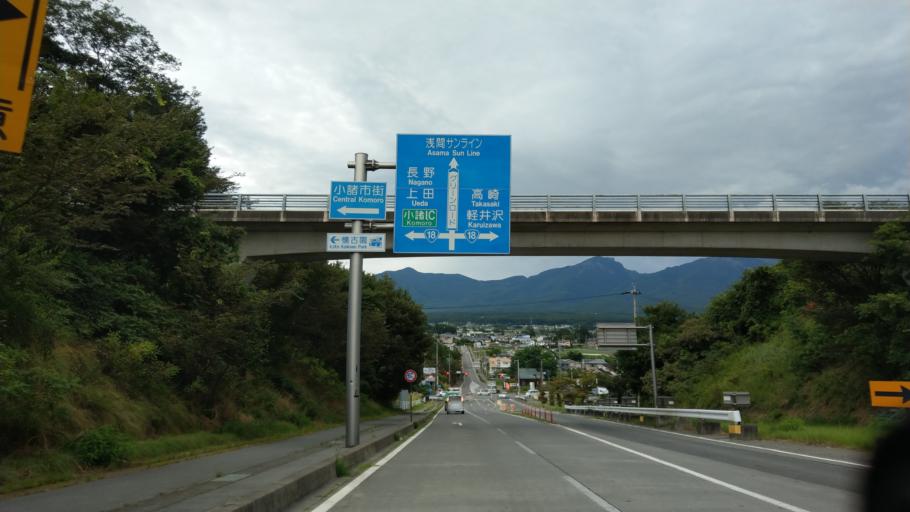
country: JP
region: Nagano
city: Komoro
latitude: 36.3116
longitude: 138.4568
